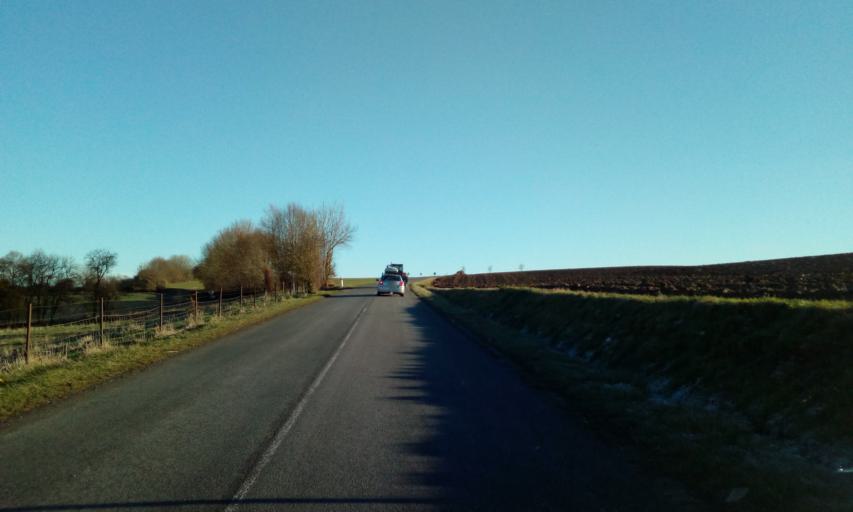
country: FR
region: Picardie
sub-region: Departement de l'Aisne
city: Rozoy-sur-Serre
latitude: 49.7031
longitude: 4.1556
